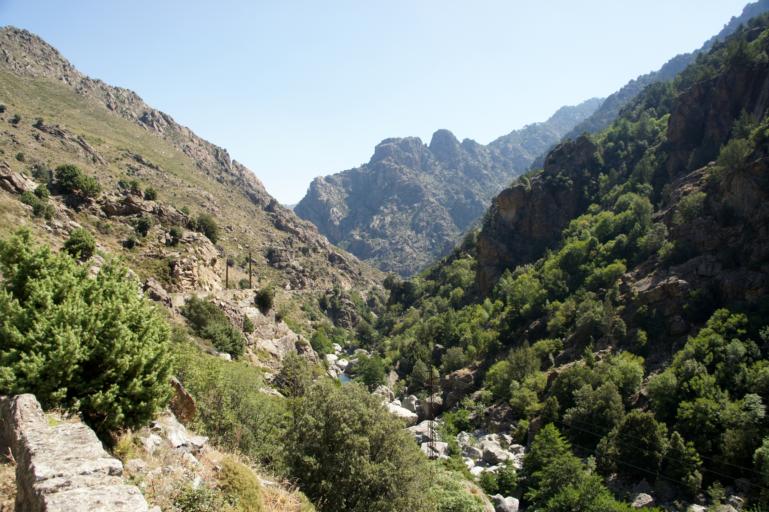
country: FR
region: Corsica
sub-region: Departement de la Haute-Corse
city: Corte
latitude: 42.3551
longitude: 9.0563
